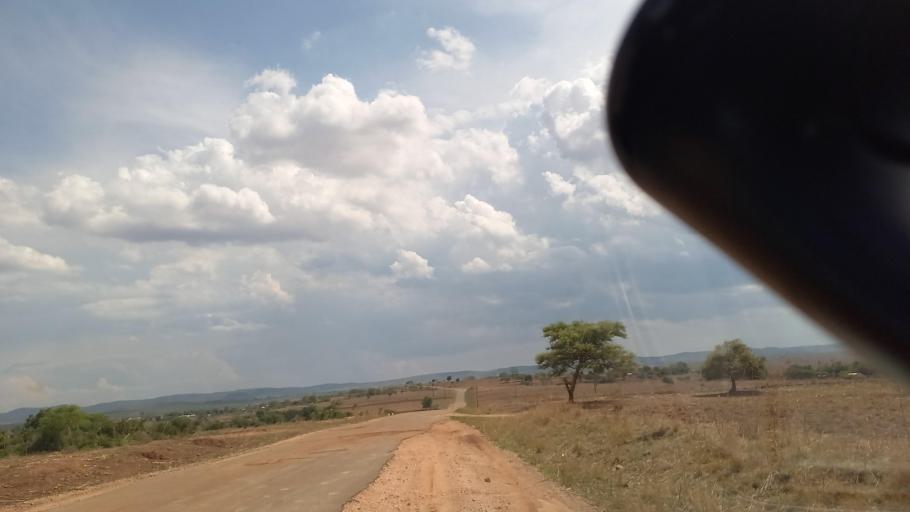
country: ZM
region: Lusaka
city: Kafue
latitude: -16.1785
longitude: 28.0886
